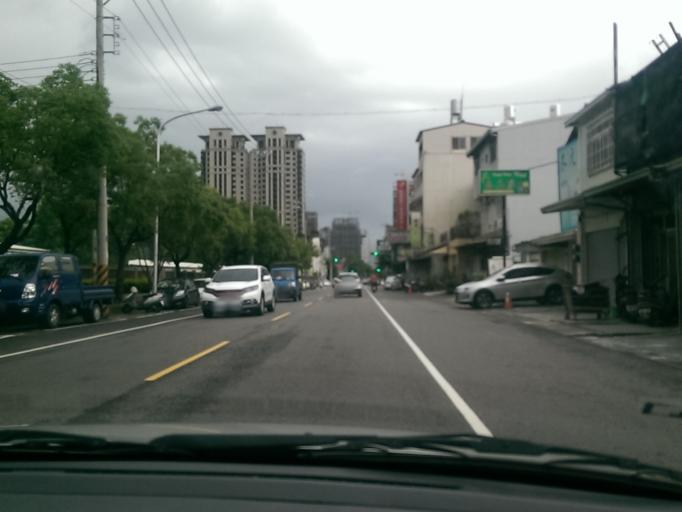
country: TW
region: Taiwan
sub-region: Taichung City
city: Taichung
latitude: 24.1667
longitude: 120.6476
